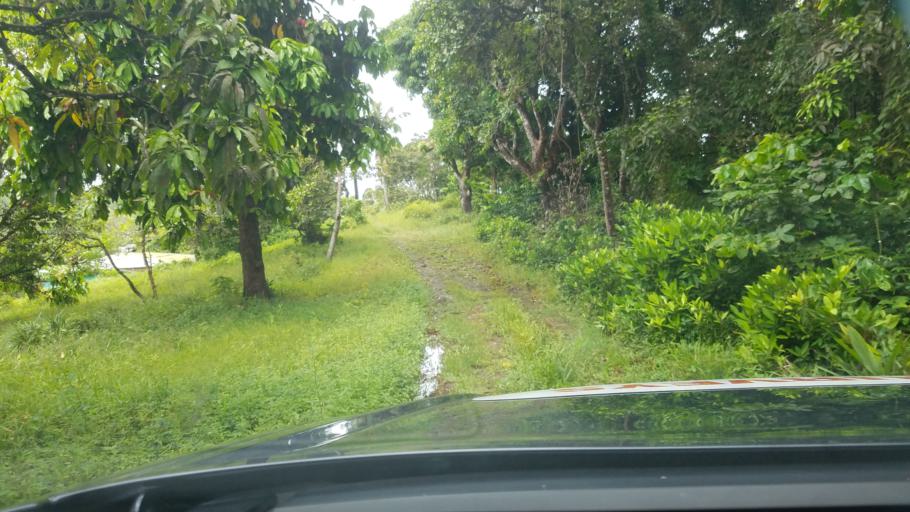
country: LC
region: Castries Quarter
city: Bisee
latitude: 13.9944
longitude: -60.9589
